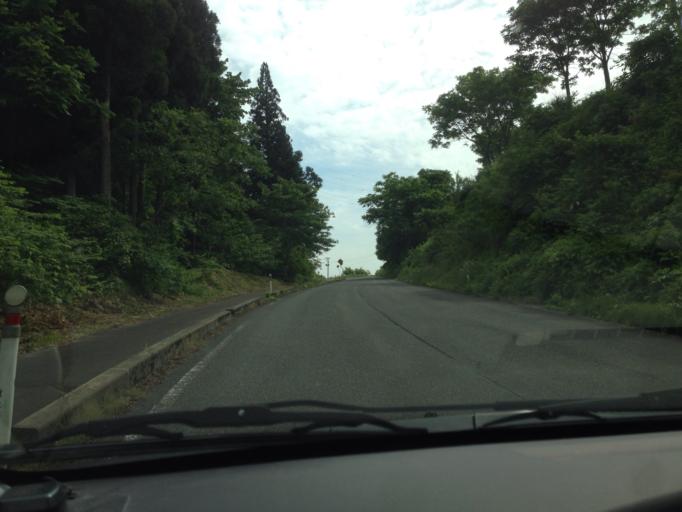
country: JP
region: Fukushima
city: Kitakata
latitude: 37.5184
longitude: 139.7216
